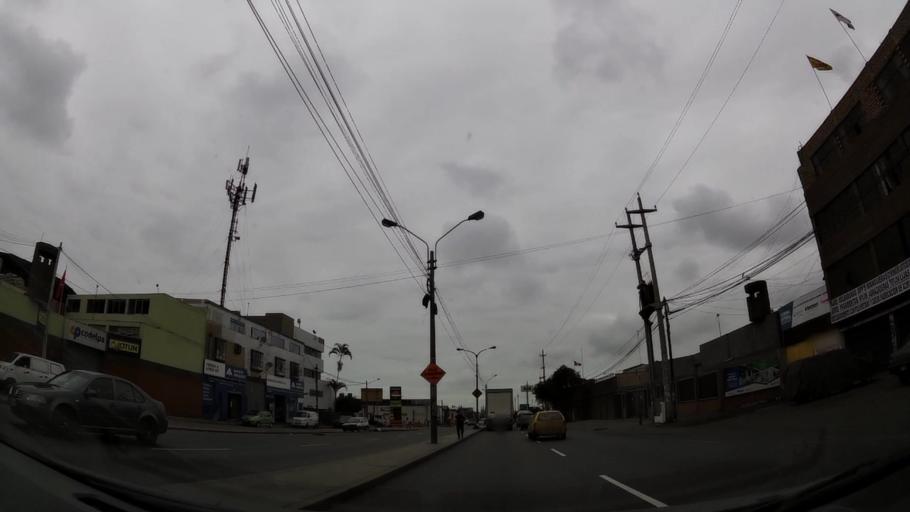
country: PE
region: Callao
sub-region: Callao
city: Callao
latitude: -12.0466
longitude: -77.0787
